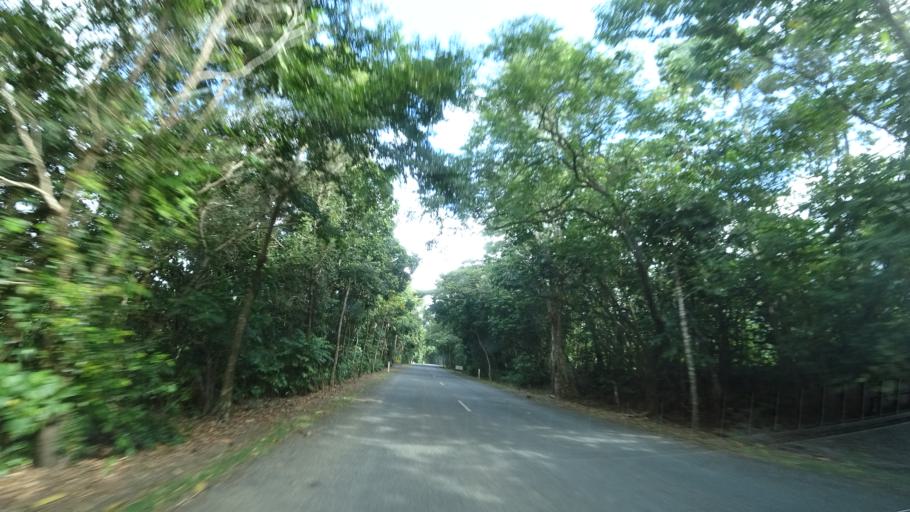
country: AU
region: Queensland
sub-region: Cairns
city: Port Douglas
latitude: -16.0938
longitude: 145.4601
